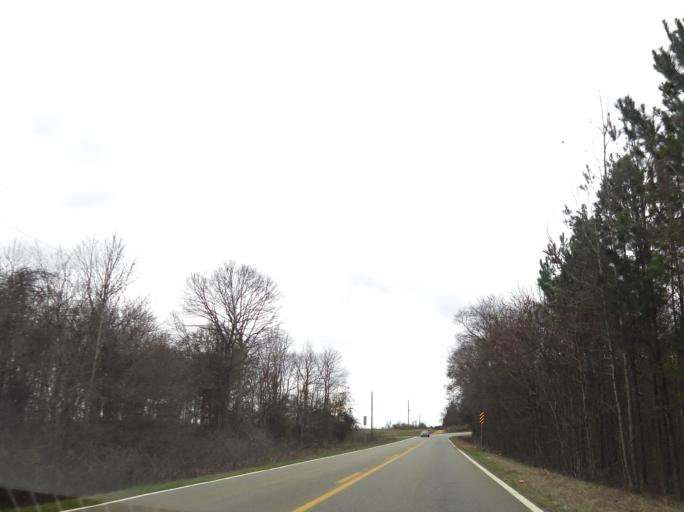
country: US
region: Georgia
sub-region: Bleckley County
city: Cochran
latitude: 32.5319
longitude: -83.3670
